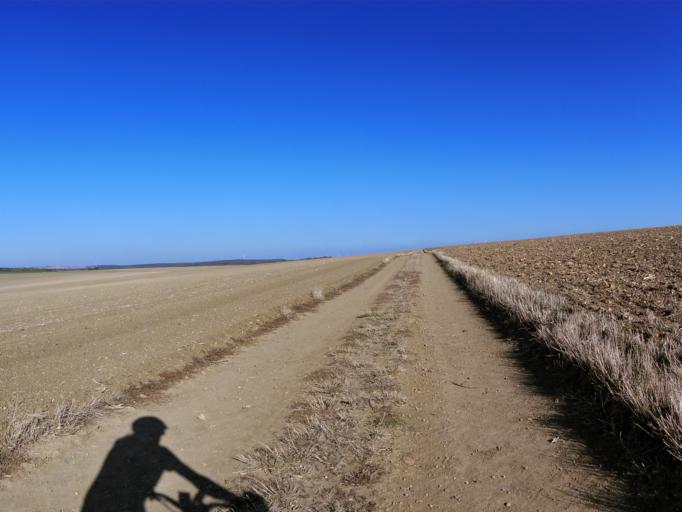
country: DE
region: Bavaria
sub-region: Regierungsbezirk Unterfranken
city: Eibelstadt
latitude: 49.7112
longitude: 9.9729
